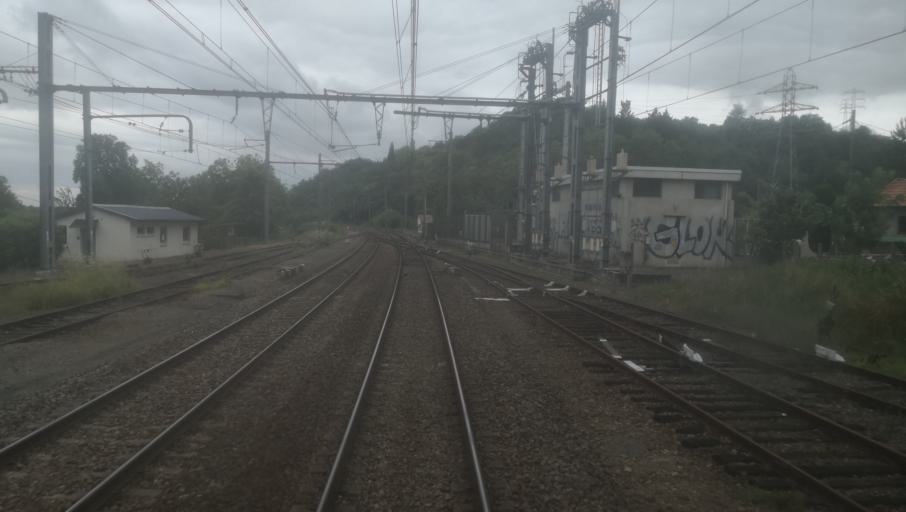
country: FR
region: Midi-Pyrenees
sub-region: Departement du Tarn-et-Garonne
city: Moissac
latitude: 44.1019
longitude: 1.0741
